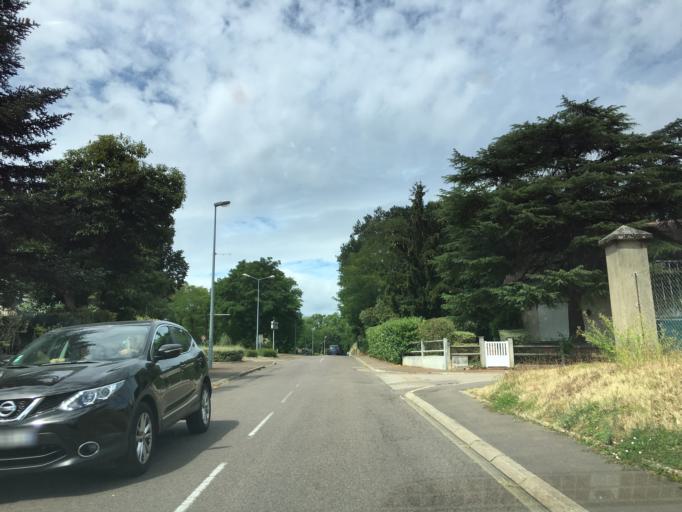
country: FR
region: Bourgogne
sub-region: Departement de l'Yonne
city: Saint-Georges-sur-Baulche
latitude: 47.8011
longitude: 3.5469
